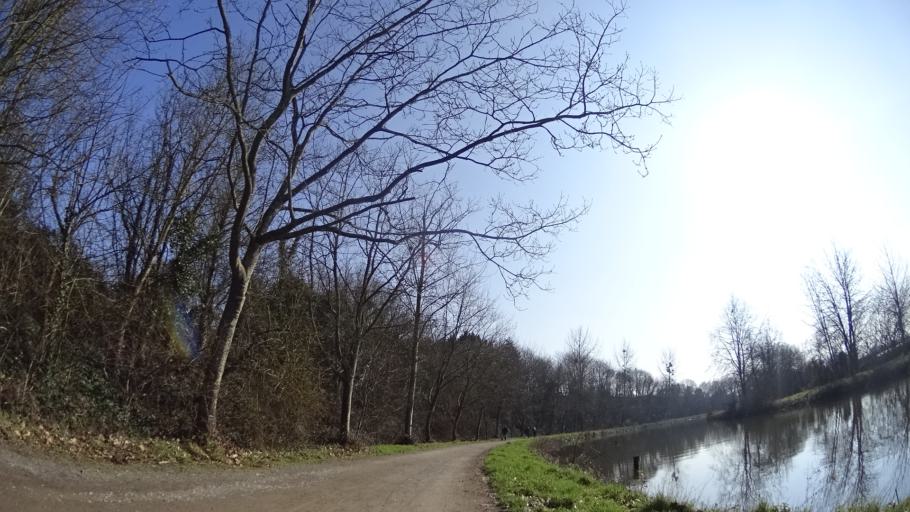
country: FR
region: Brittany
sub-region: Departement d'Ille-et-Vilaine
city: Saint-Gregoire
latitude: 48.1404
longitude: -1.6736
